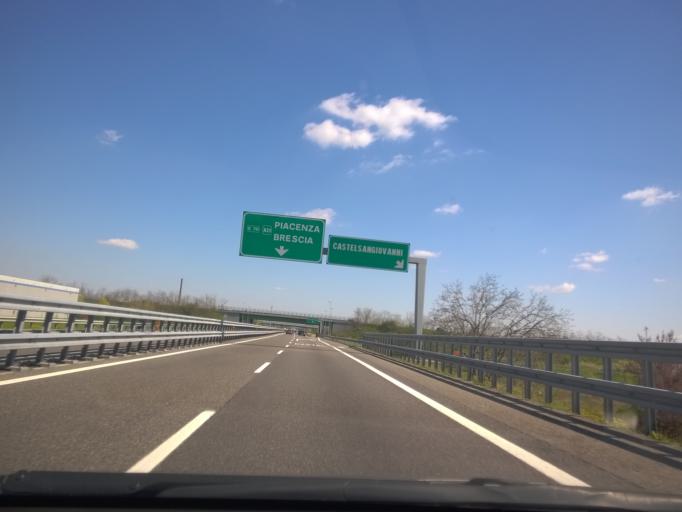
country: IT
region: Emilia-Romagna
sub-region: Provincia di Piacenza
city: Castel San Giovanni
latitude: 45.0762
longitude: 9.4459
